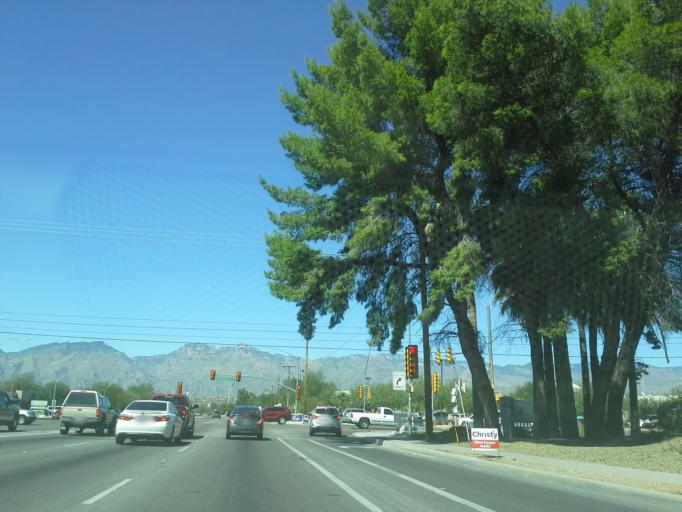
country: US
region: Arizona
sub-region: Pima County
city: Tucson
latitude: 32.2349
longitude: -110.8409
